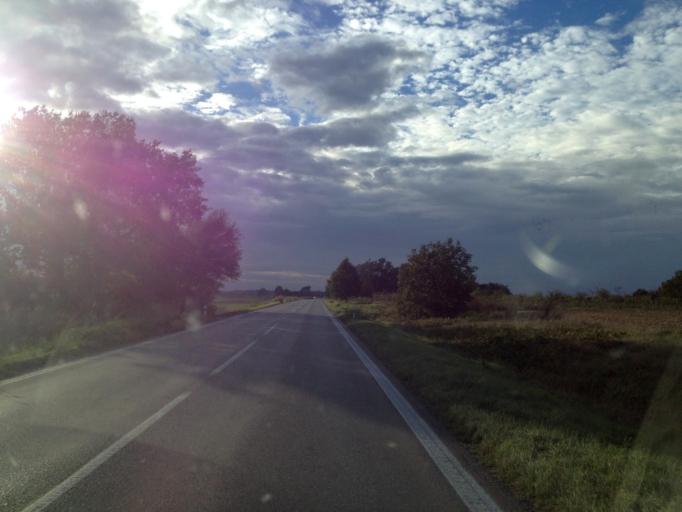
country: HU
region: Komarom-Esztergom
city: Almasfuzito
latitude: 47.7589
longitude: 18.2008
